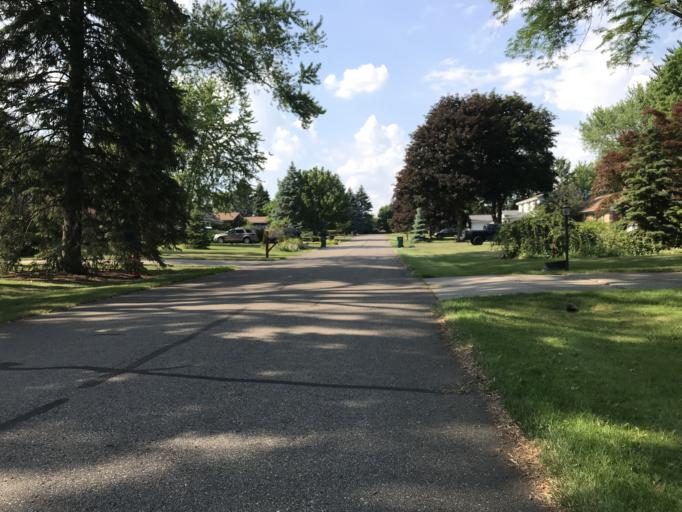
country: US
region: Michigan
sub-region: Oakland County
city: Farmington
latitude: 42.4668
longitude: -83.3877
